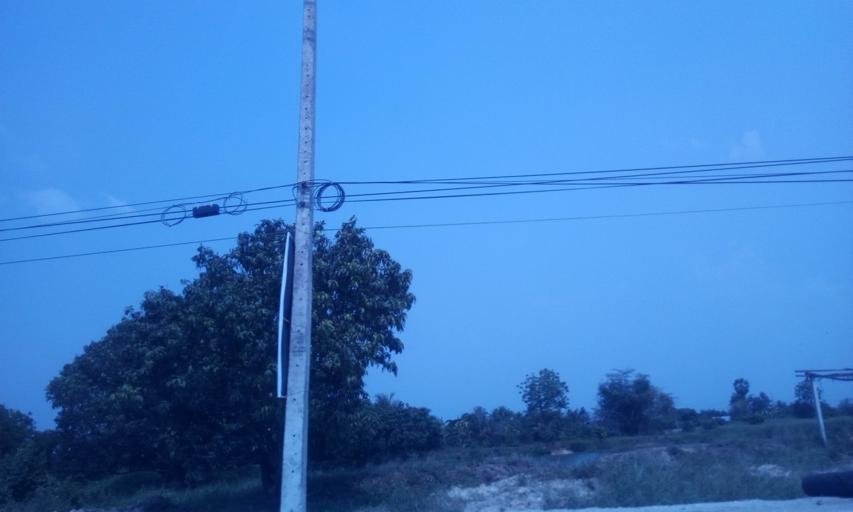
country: TH
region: Chon Buri
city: Phanat Nikhom
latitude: 13.4172
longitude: 101.1876
